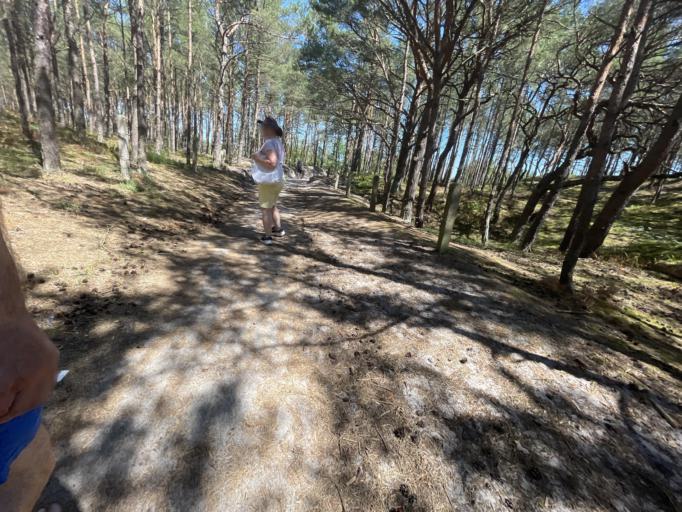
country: PL
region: Pomeranian Voivodeship
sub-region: Powiat pucki
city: Jastarnia
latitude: 54.6948
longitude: 18.6952
